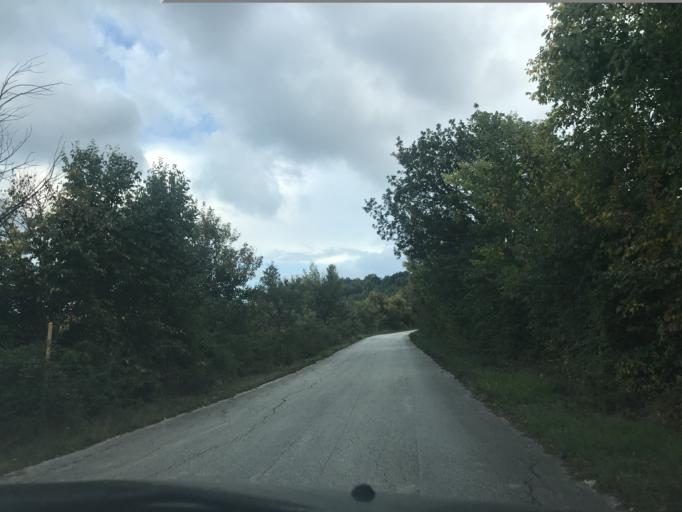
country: IT
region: Molise
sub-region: Provincia di Campobasso
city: Duronia
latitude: 41.6678
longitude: 14.4602
